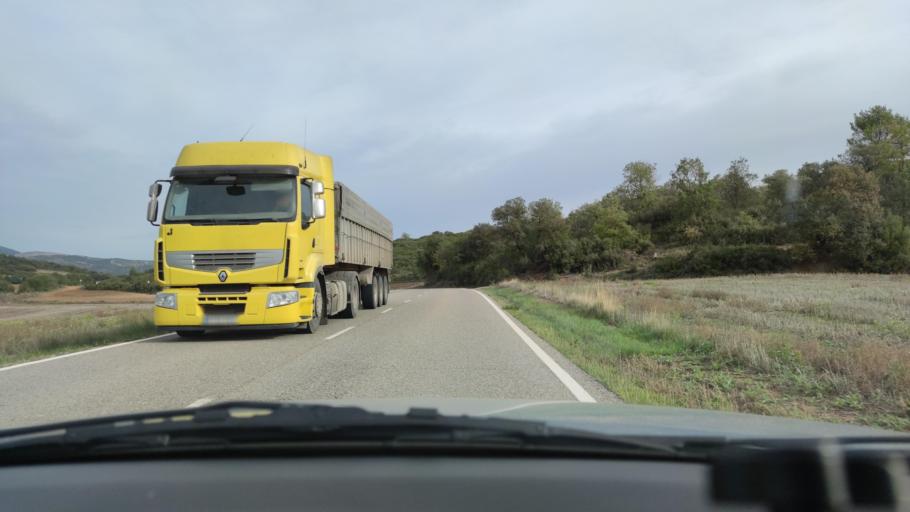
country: ES
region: Catalonia
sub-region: Provincia de Lleida
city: Artesa de Segre
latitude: 41.9413
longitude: 1.0597
